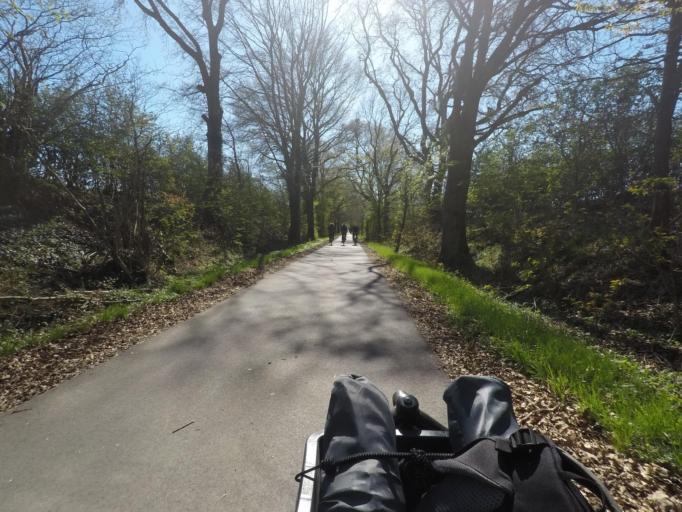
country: DE
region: Schleswig-Holstein
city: Braak
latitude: 53.6037
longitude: 10.2774
